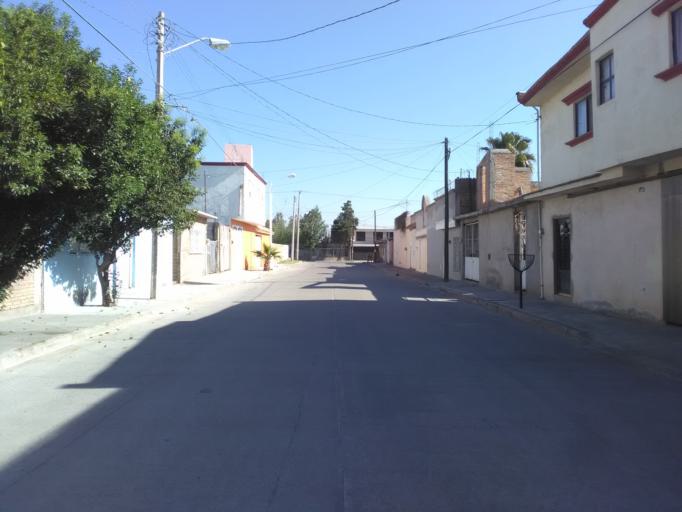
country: MX
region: Durango
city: Victoria de Durango
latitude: 24.0126
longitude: -104.6390
